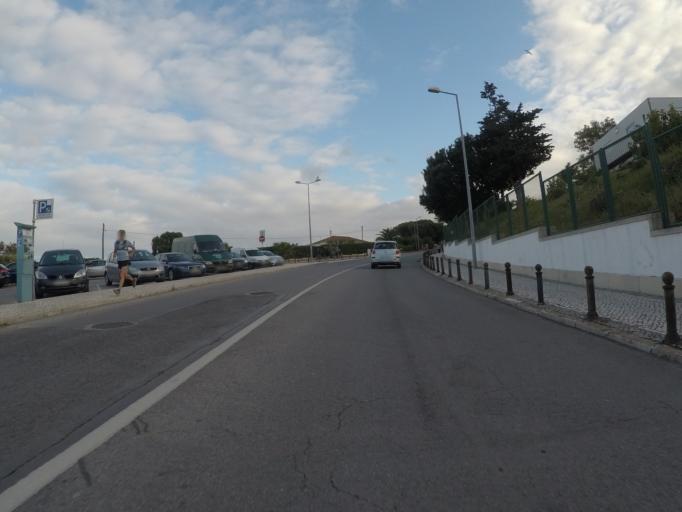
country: PT
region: Faro
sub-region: Lagos
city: Lagos
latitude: 37.0971
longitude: -8.6687
